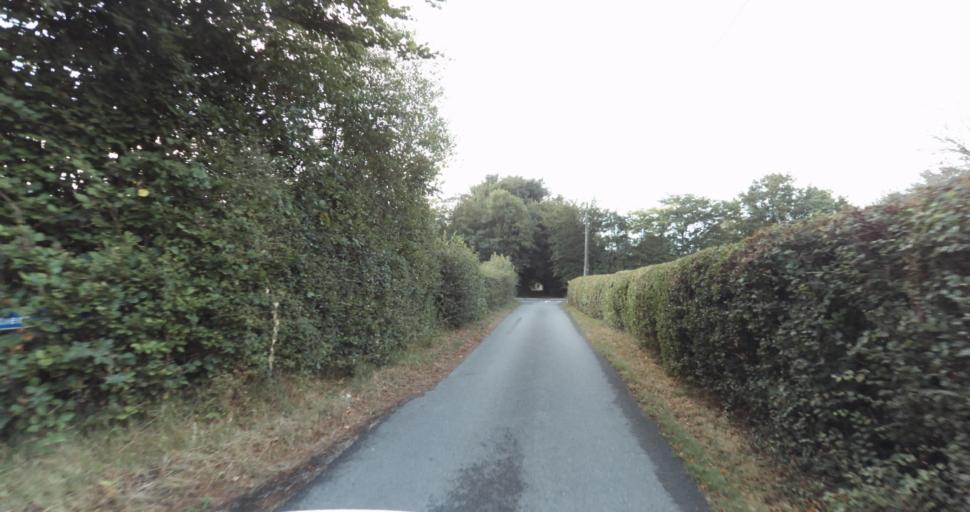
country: FR
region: Lower Normandy
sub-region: Departement de l'Orne
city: Vimoutiers
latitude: 48.9334
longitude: 0.2195
